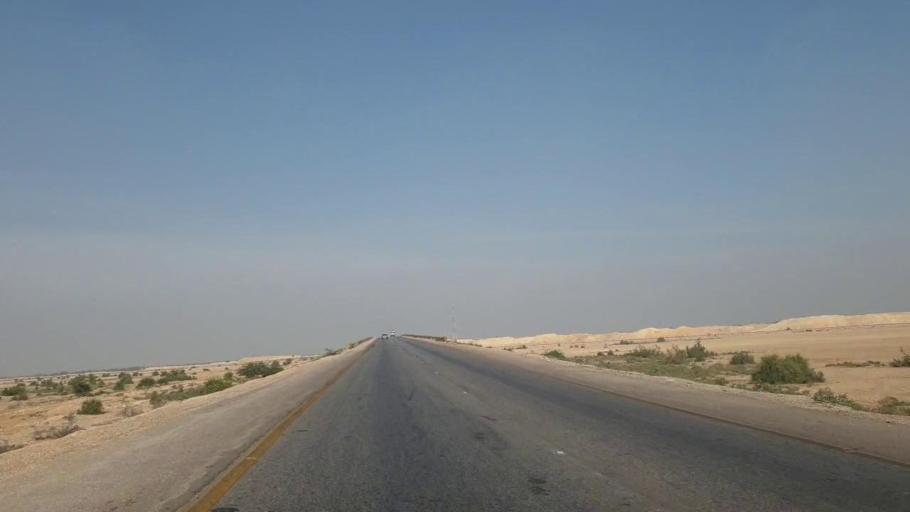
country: PK
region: Sindh
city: Hala
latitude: 25.8568
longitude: 68.2571
